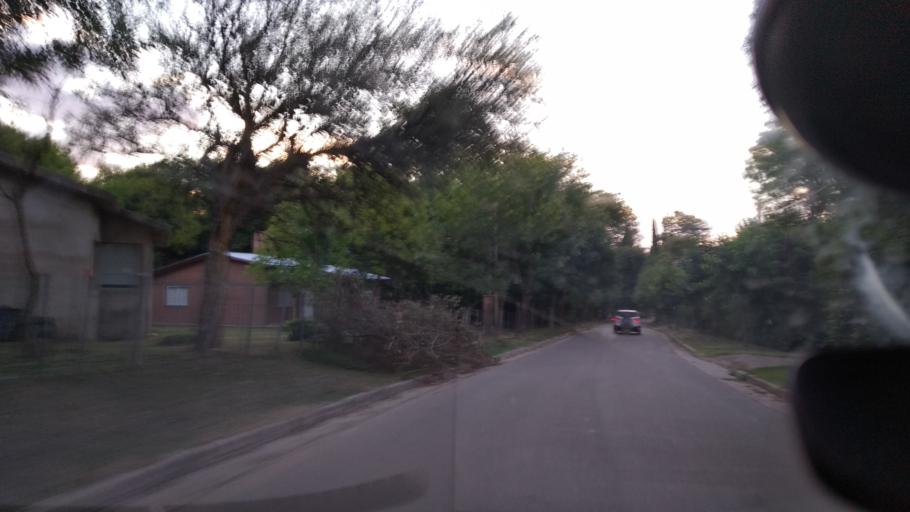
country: AR
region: Cordoba
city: Villa Las Rosas
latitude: -31.9455
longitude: -65.0579
